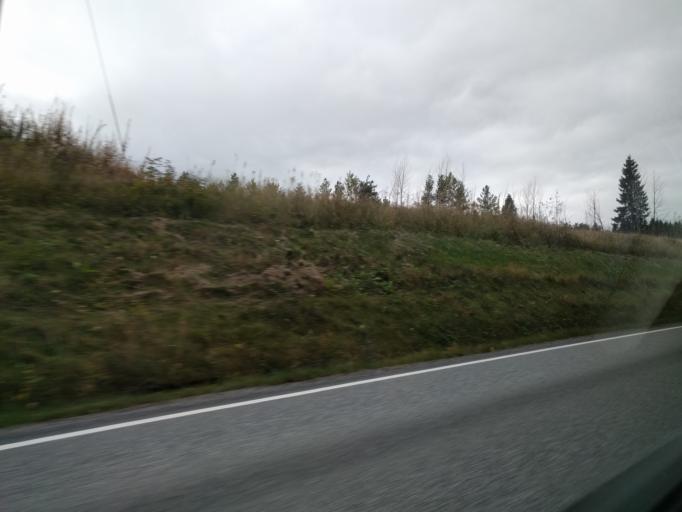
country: NO
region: Aust-Agder
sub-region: Iveland
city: Birketveit
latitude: 58.3904
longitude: 7.7432
